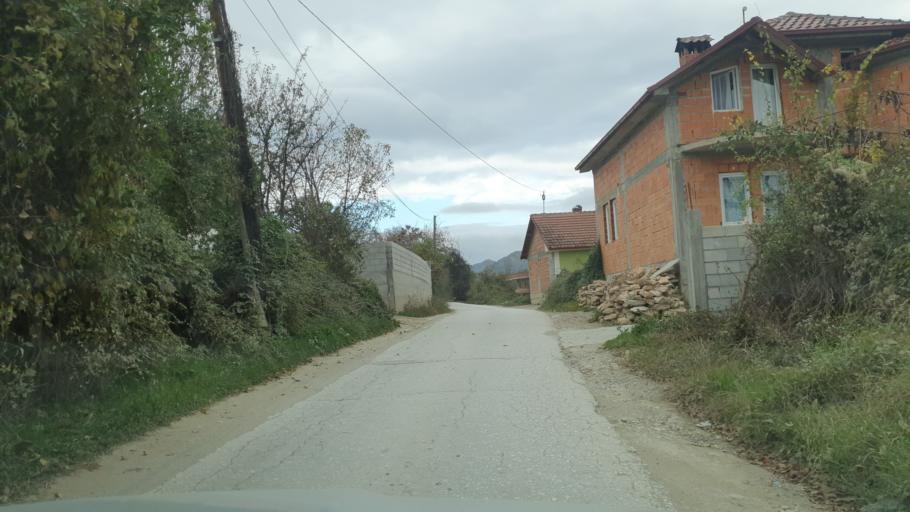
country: MK
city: Kondovo
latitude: 42.0340
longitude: 21.2829
